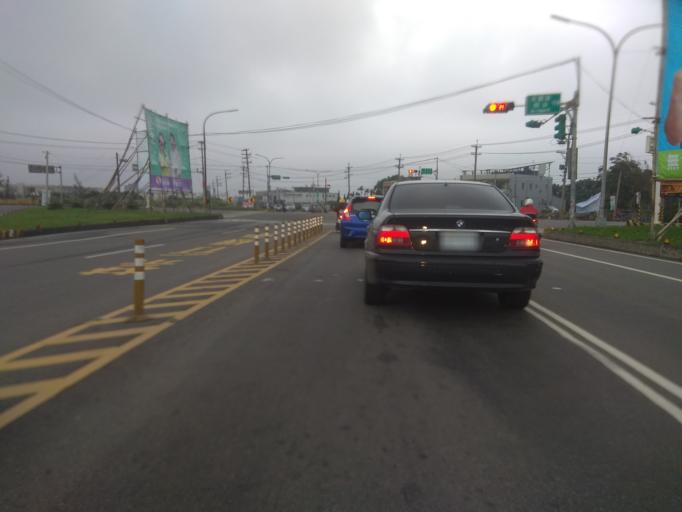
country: TW
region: Taiwan
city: Taoyuan City
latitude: 25.0336
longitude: 121.0953
